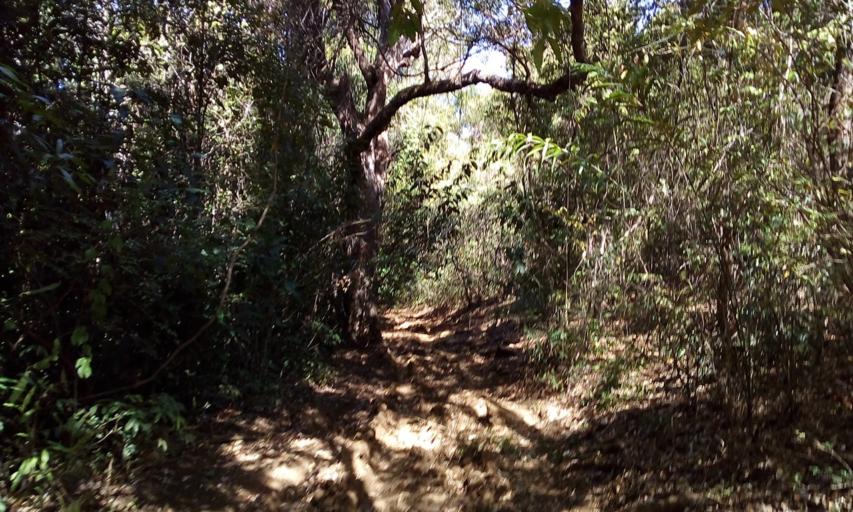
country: MG
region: Melaky
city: Mahabe
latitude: -16.3815
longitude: 45.3430
